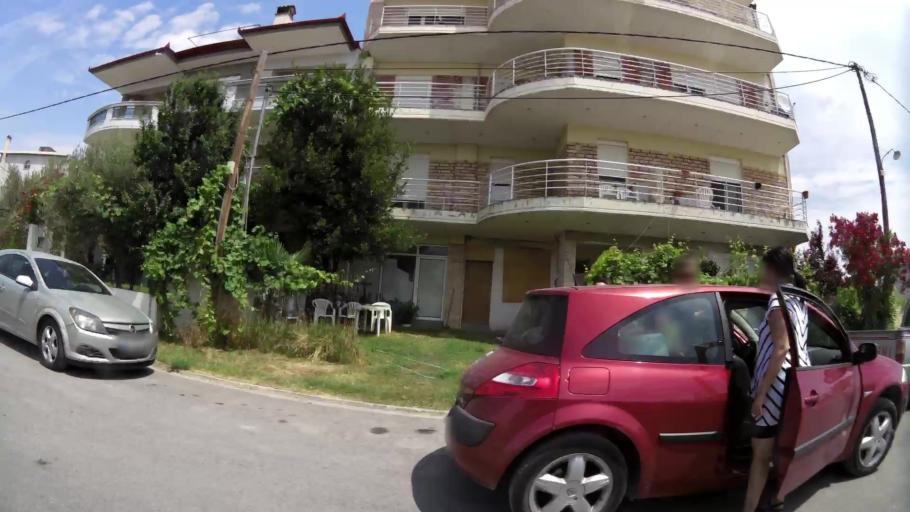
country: GR
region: Central Macedonia
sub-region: Nomos Pierias
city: Katerini
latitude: 40.2616
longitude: 22.5171
